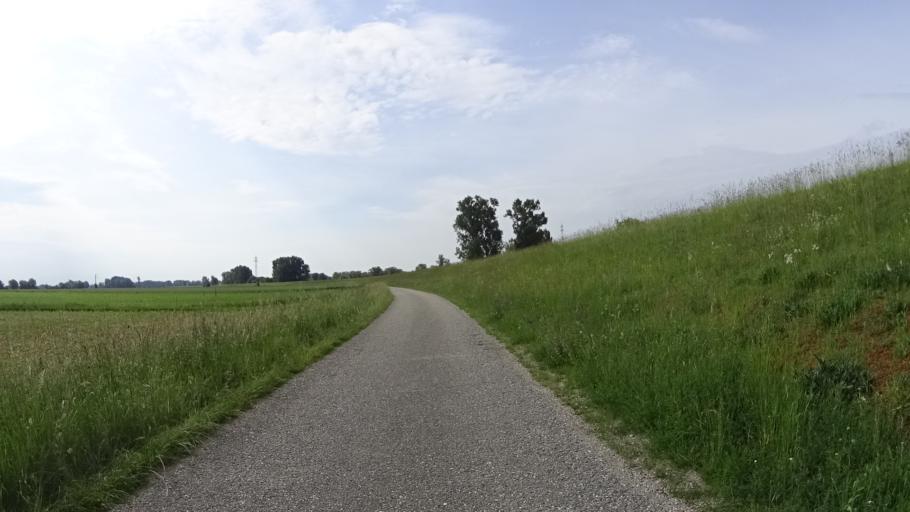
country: DE
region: Bavaria
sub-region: Lower Bavaria
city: Irlbach
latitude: 48.8441
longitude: 12.7677
